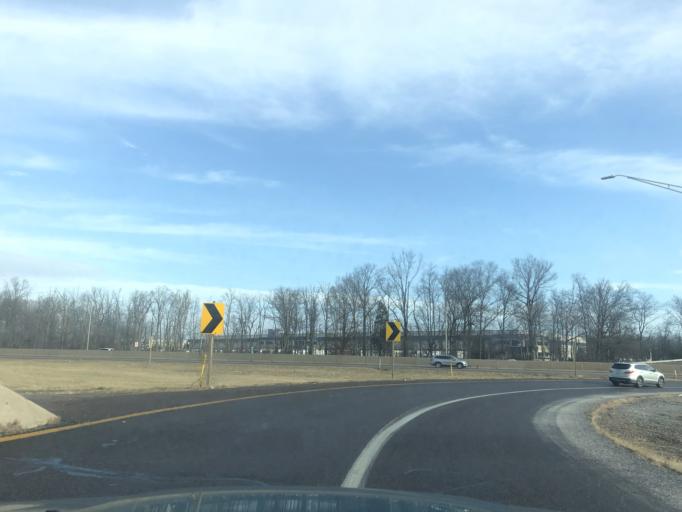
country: US
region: Pennsylvania
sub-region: Bucks County
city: Spinnerstown
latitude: 40.4383
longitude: -75.4276
